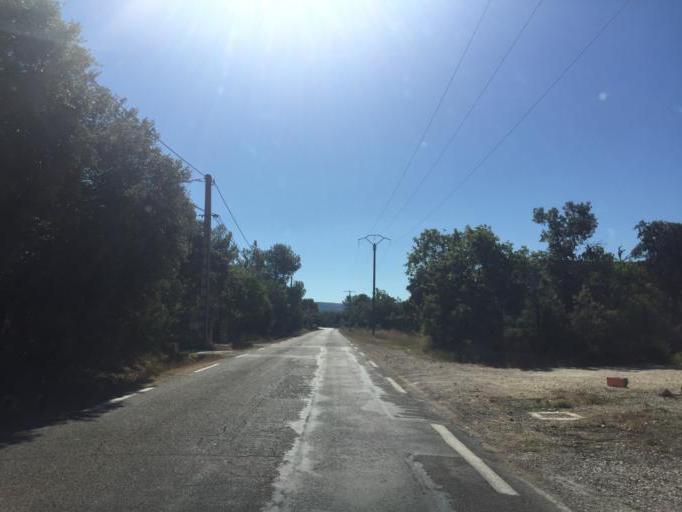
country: FR
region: Provence-Alpes-Cote d'Azur
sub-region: Departement du Vaucluse
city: Saint-Didier
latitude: 44.0218
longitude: 5.1161
